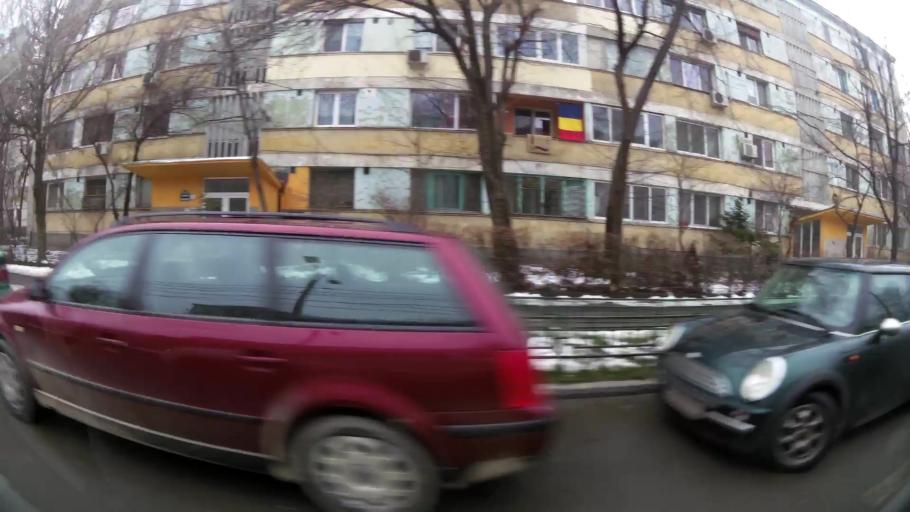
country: RO
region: Ilfov
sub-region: Comuna Chiajna
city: Rosu
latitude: 44.4609
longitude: 26.0404
